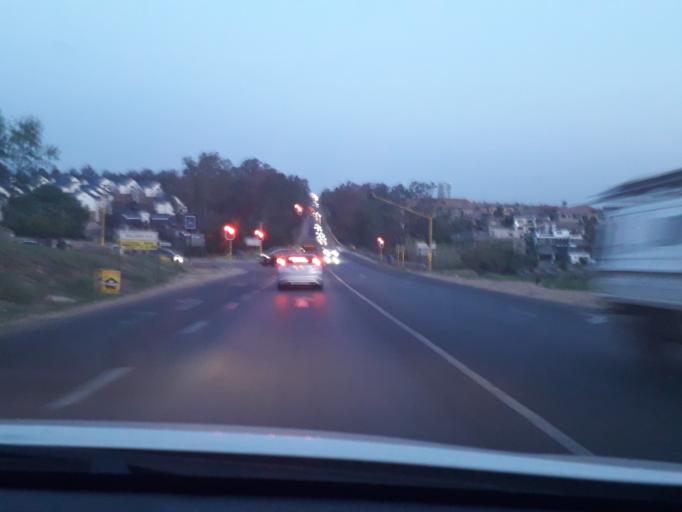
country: ZA
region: Gauteng
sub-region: City of Johannesburg Metropolitan Municipality
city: Midrand
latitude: -25.9996
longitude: 28.0810
